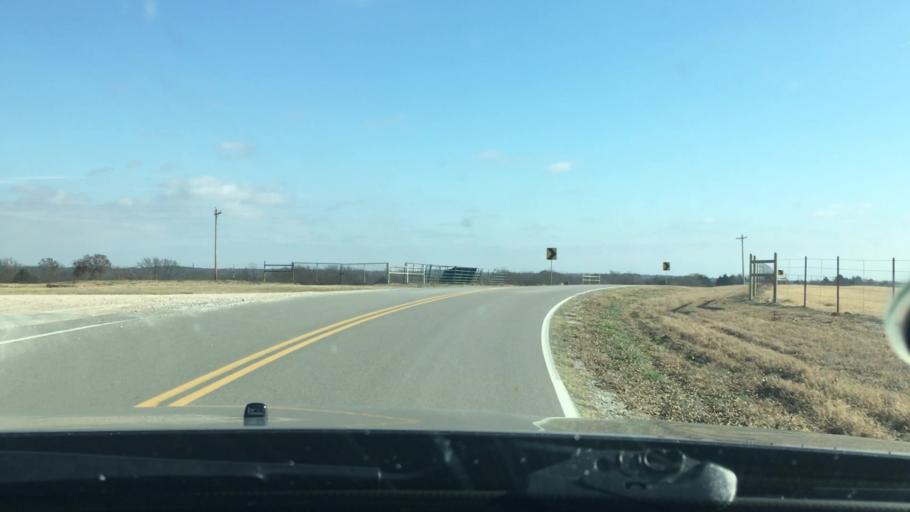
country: US
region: Oklahoma
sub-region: Marshall County
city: Oakland
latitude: 34.0254
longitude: -96.9321
